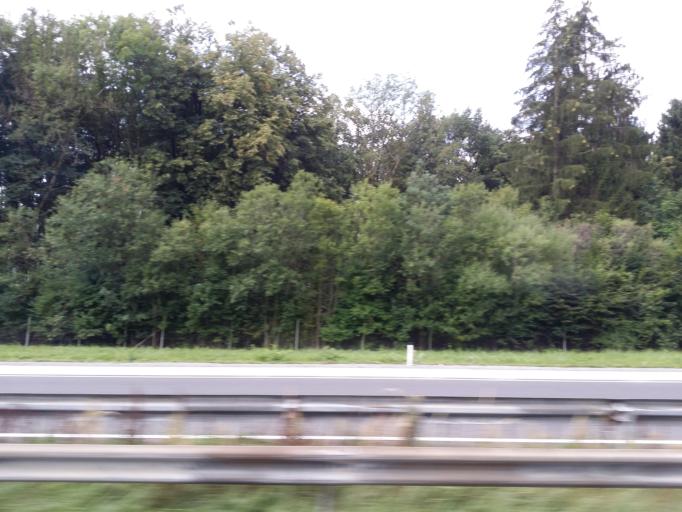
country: SI
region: Kranj
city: Britof
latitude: 46.2444
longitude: 14.3951
